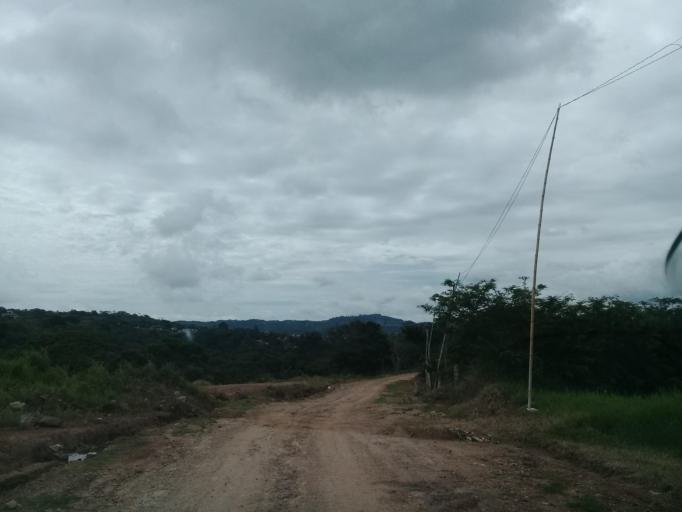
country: MX
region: Veracruz
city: El Castillo
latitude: 19.5533
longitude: -96.8773
